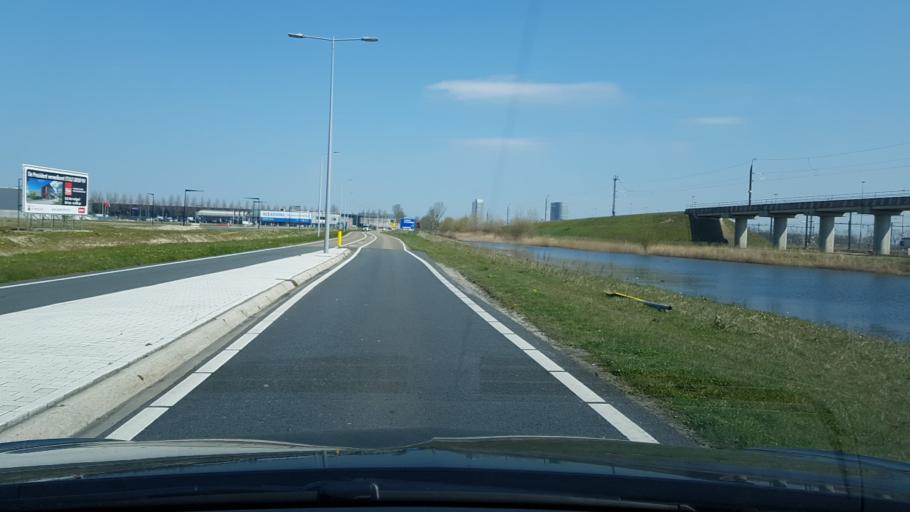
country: NL
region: North Holland
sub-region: Gemeente Haarlemmermeer
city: Hoofddorp
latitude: 52.2822
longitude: 4.6778
